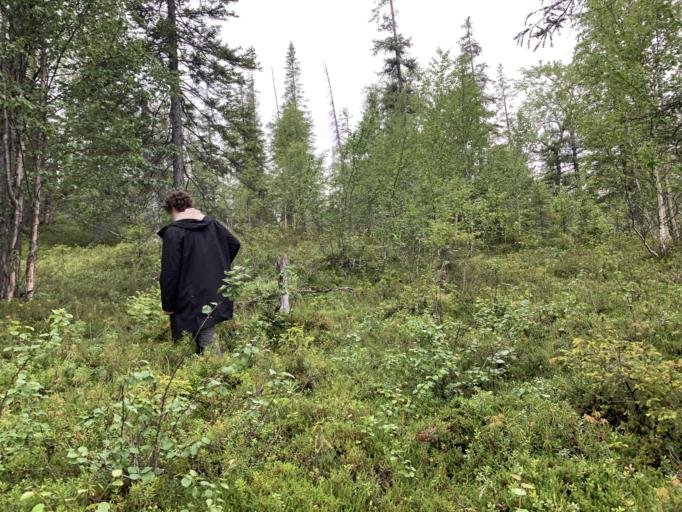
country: RU
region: Murmansk
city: Monchegorsk
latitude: 67.6945
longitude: 33.0605
